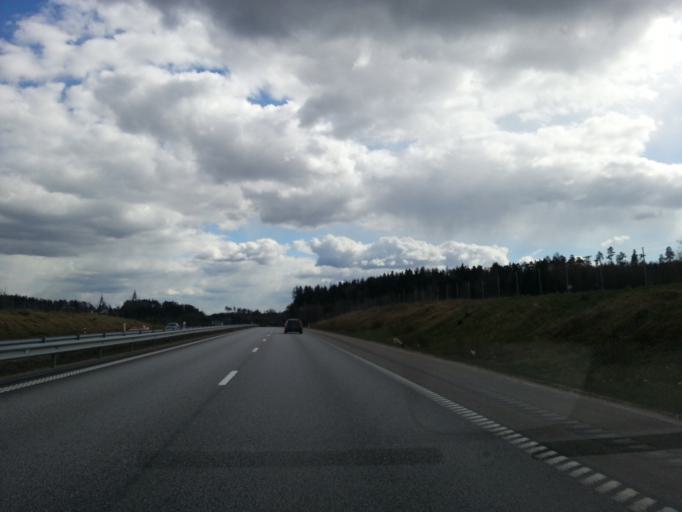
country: SE
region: Vaestra Goetaland
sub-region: Uddevalla Kommun
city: Uddevalla
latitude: 58.3427
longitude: 11.8235
